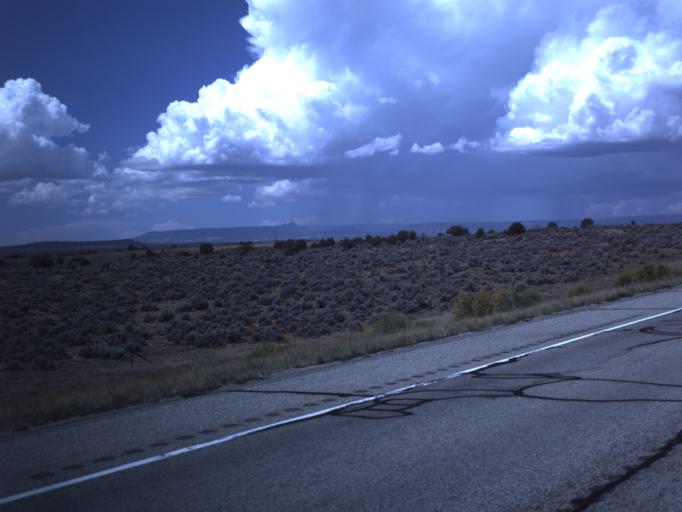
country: US
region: Utah
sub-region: San Juan County
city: Blanding
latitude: 37.5030
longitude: -109.4870
